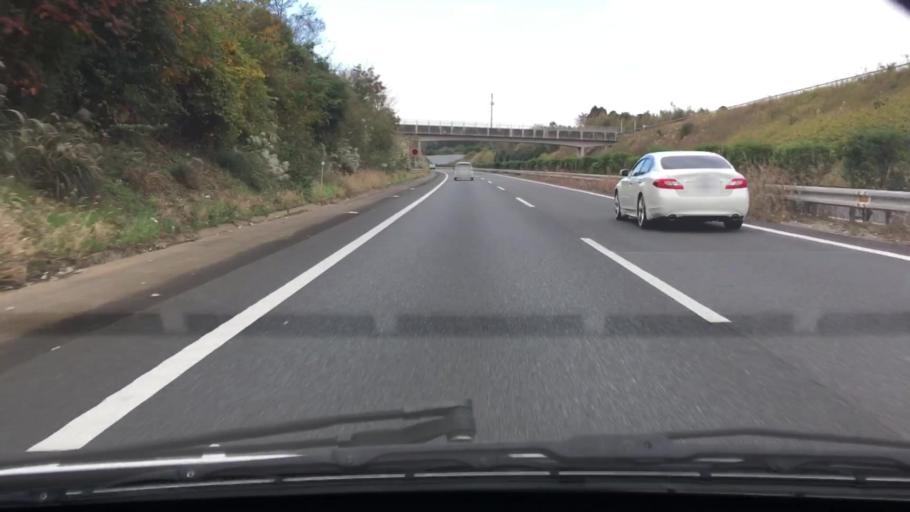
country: JP
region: Chiba
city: Ichihara
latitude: 35.4247
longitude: 140.0263
